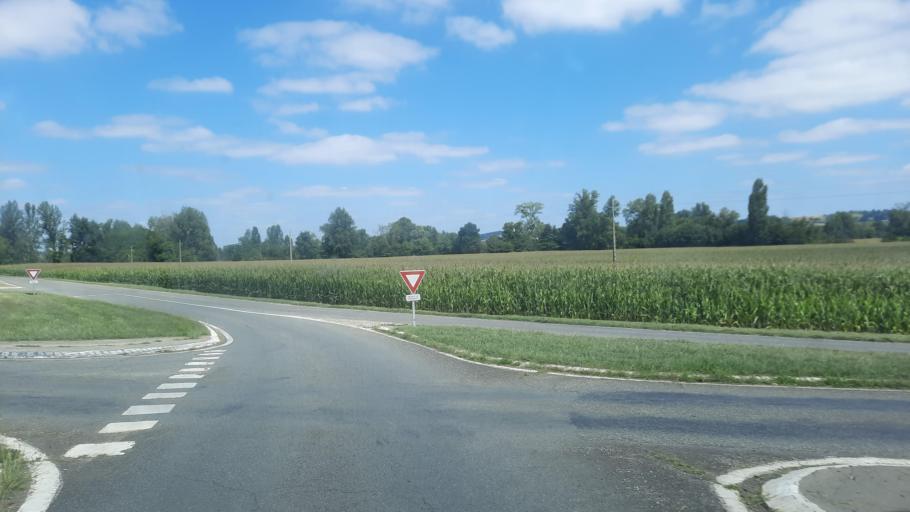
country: FR
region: Midi-Pyrenees
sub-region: Departement du Gers
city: Lombez
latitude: 43.4335
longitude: 0.8454
